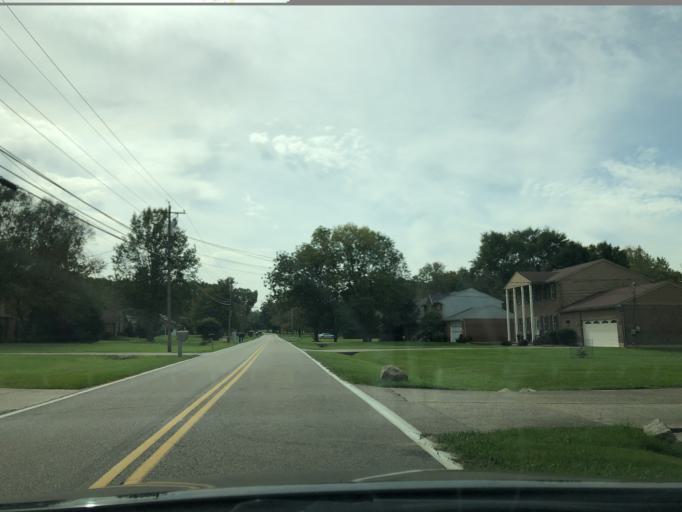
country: US
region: Ohio
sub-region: Hamilton County
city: The Village of Indian Hill
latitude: 39.2291
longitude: -84.3007
